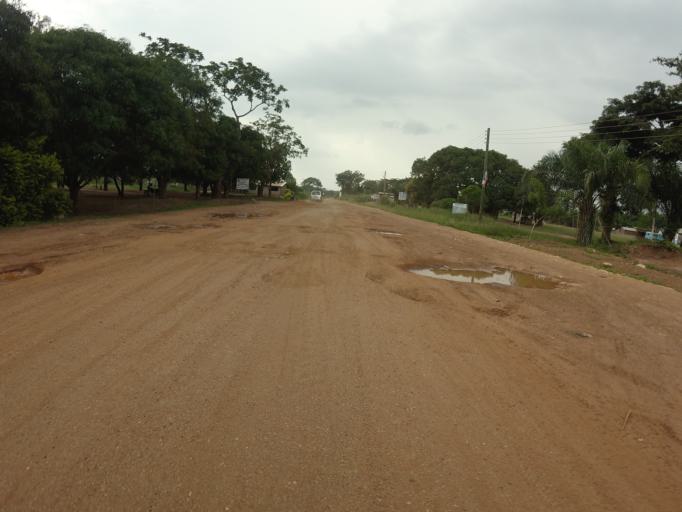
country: GH
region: Volta
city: Kpandu
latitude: 7.0029
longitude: 0.4344
